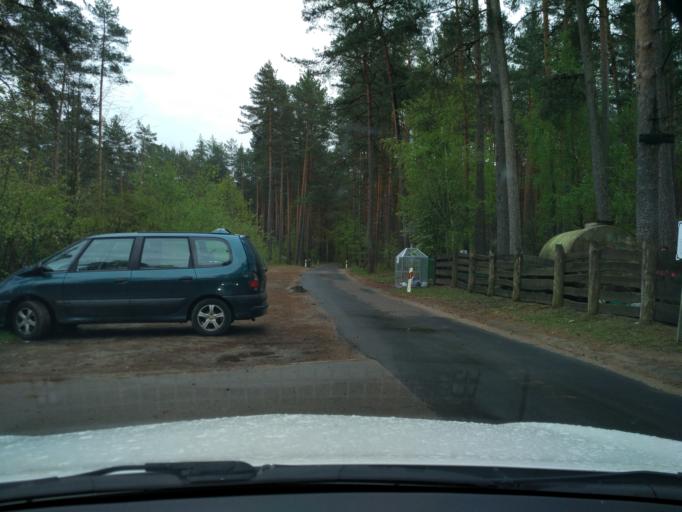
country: LT
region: Vilnius County
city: Rasos
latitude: 54.7425
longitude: 25.3955
